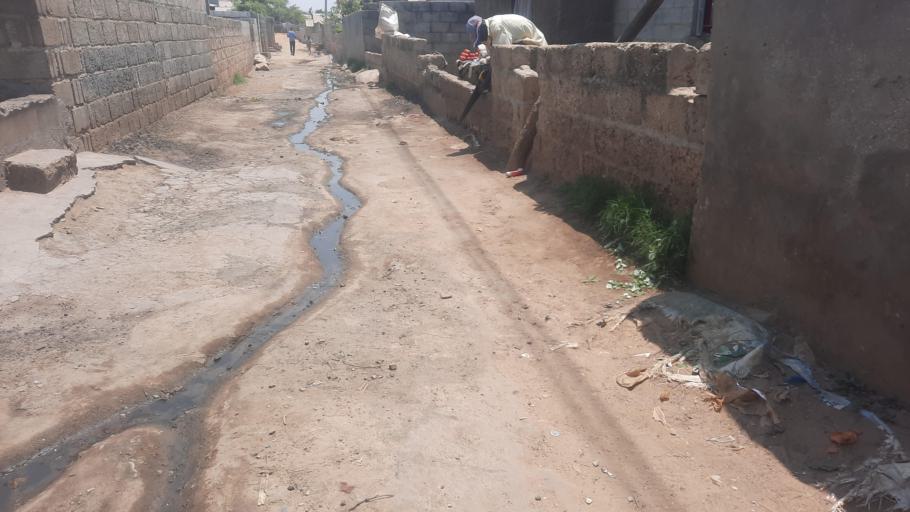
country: ZM
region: Lusaka
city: Lusaka
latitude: -15.3997
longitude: 28.3755
